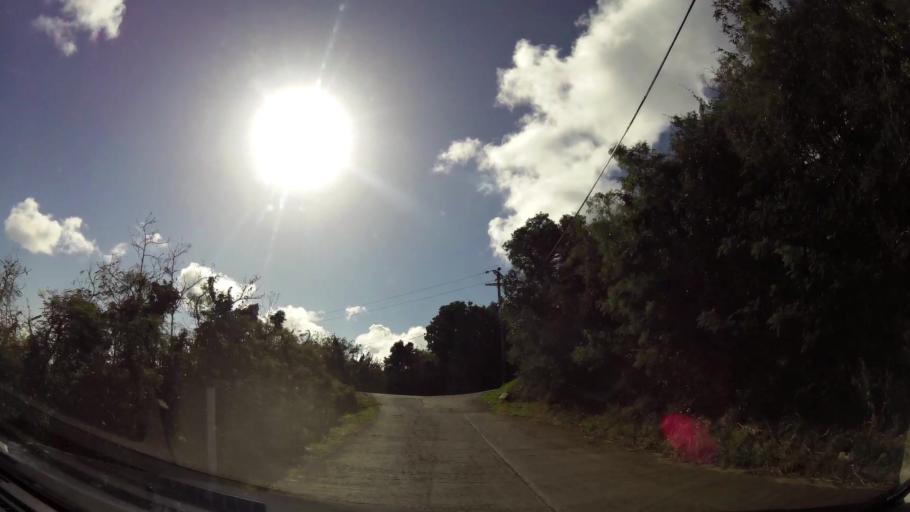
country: VG
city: Tortola
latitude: 18.4327
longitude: -64.5770
